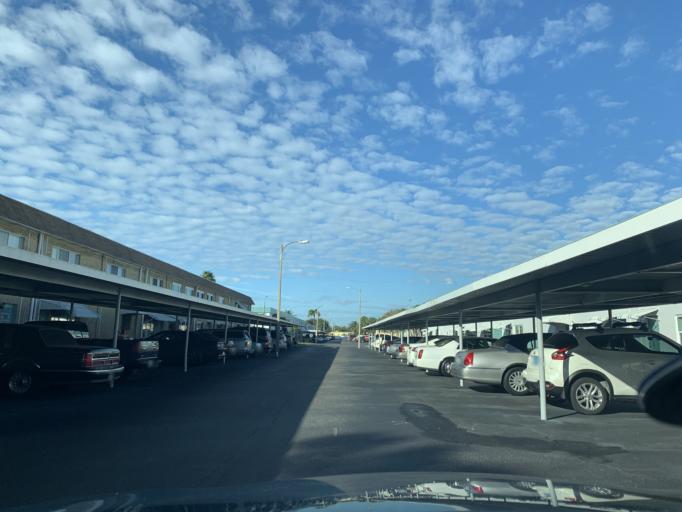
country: US
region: Florida
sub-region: Pinellas County
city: Bay Pines
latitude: 27.8199
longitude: -82.7499
